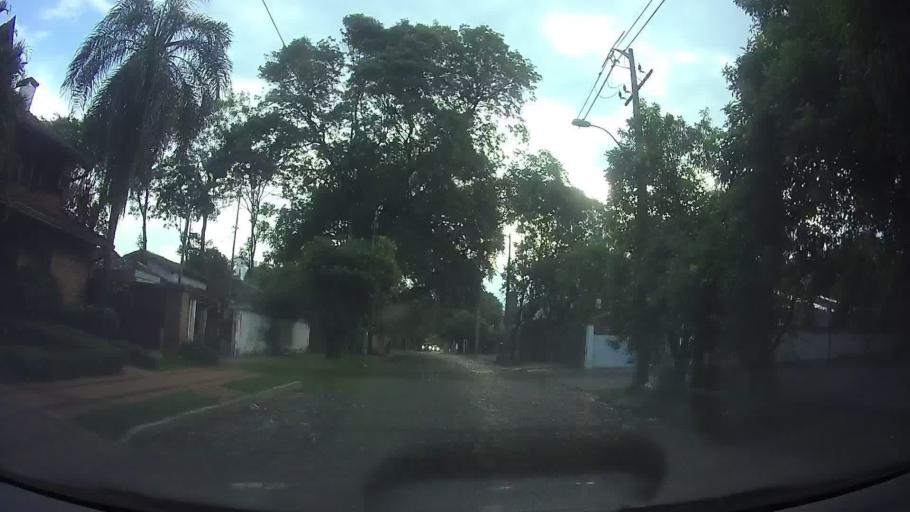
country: PY
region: Asuncion
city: Asuncion
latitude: -25.2791
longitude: -57.5662
